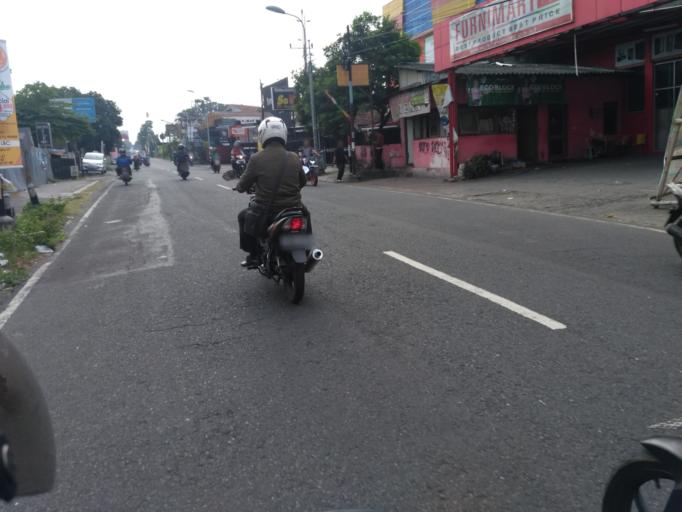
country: ID
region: Daerah Istimewa Yogyakarta
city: Melati
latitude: -7.7310
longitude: 110.3973
